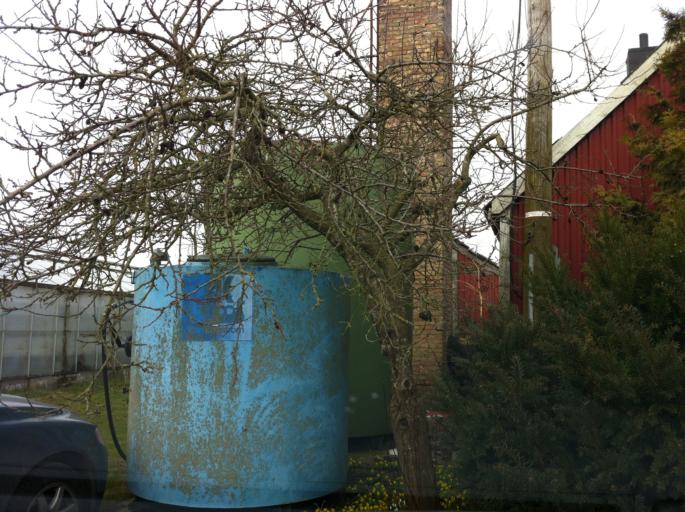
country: SE
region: Skane
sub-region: Svalovs Kommun
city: Teckomatorp
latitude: 55.8394
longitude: 13.0961
